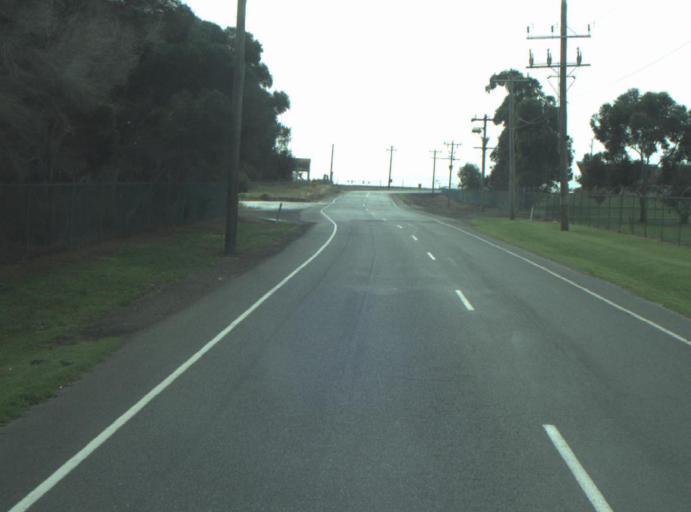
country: AU
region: Victoria
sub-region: Greater Geelong
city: Bell Park
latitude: -38.0843
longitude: 144.3811
